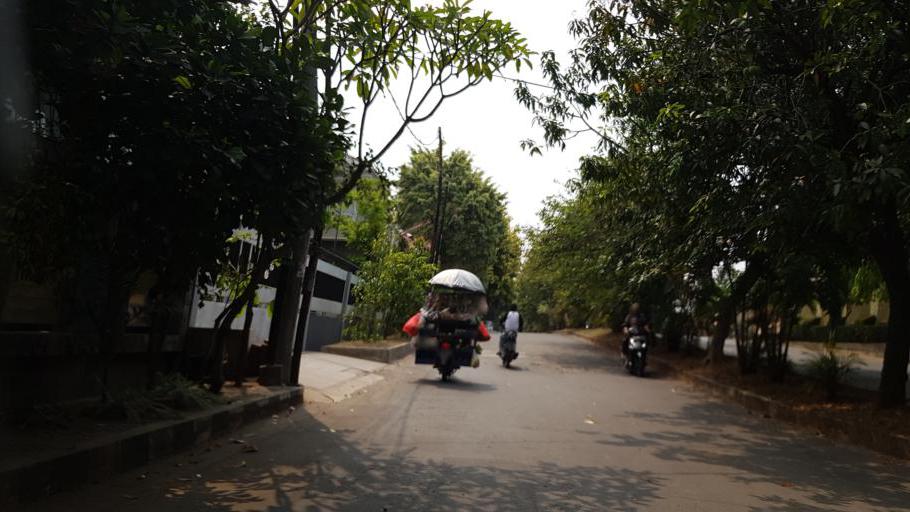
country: ID
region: West Java
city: Pamulang
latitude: -6.3272
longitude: 106.7871
